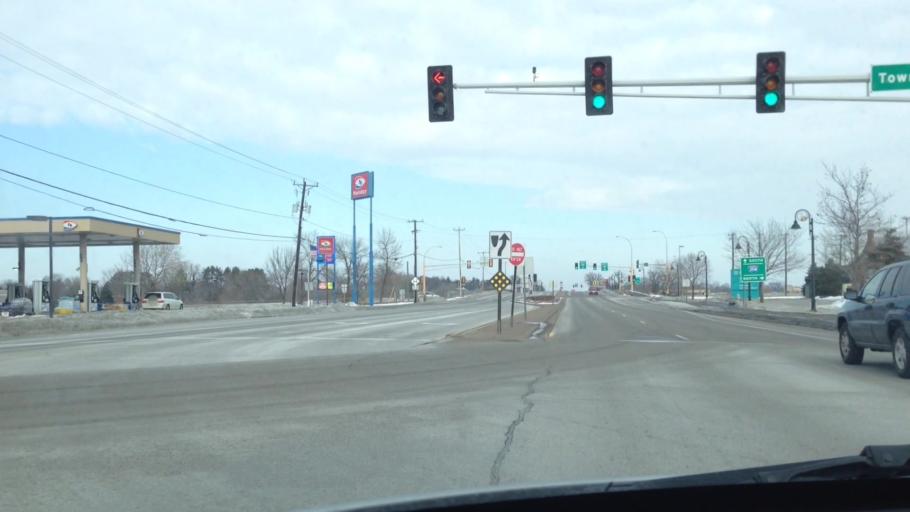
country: US
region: Minnesota
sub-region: Anoka County
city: Lino Lakes
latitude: 45.1775
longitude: -93.1147
